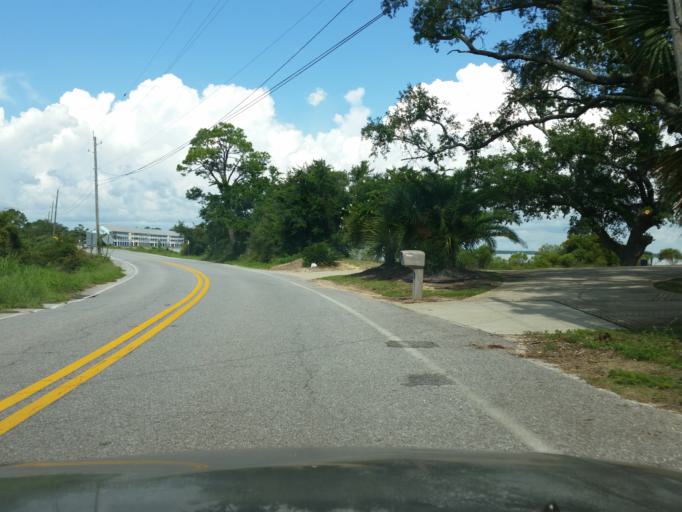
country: US
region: Alabama
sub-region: Baldwin County
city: Orange Beach
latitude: 30.3143
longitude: -87.4689
